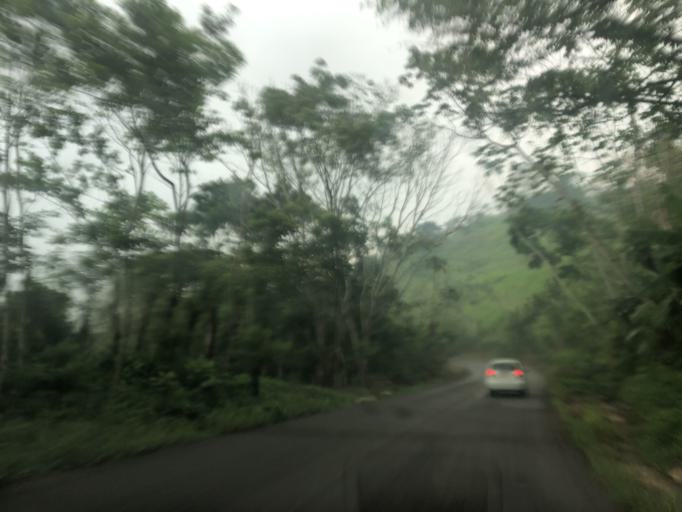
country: MX
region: Chiapas
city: Pichucalco
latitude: 17.5402
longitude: -93.1354
